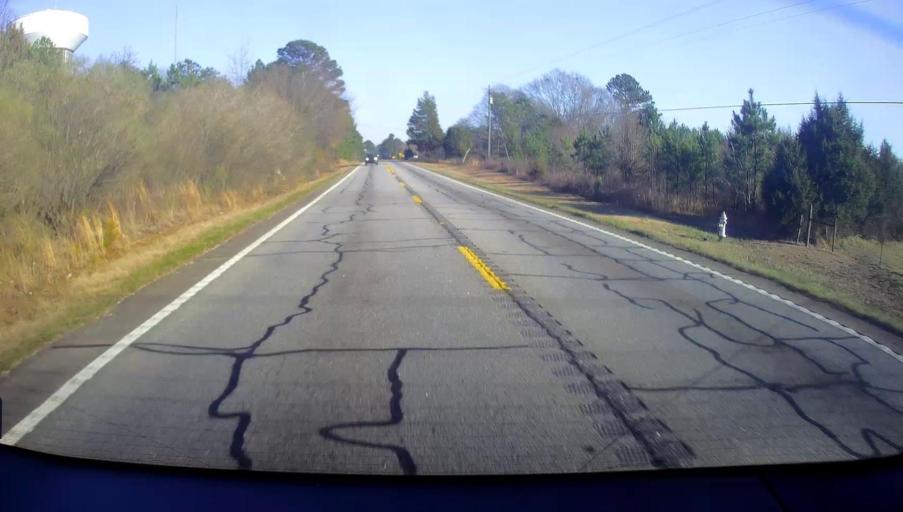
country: US
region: Georgia
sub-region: Henry County
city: Hampton
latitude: 33.4209
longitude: -84.2663
